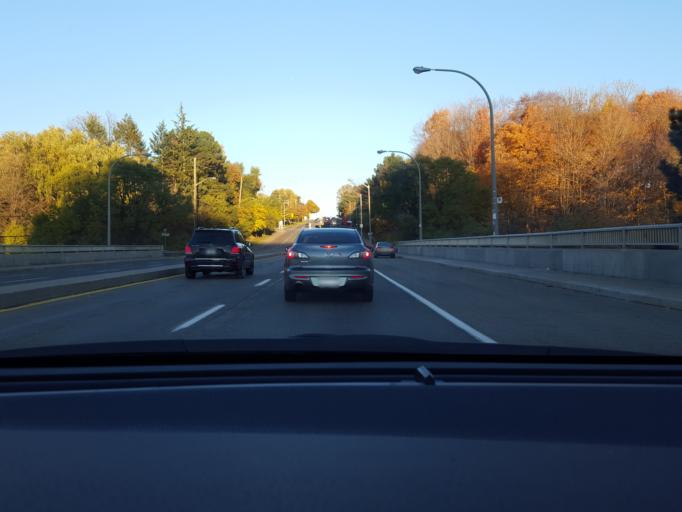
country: CA
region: Ontario
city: Willowdale
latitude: 43.7563
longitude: -79.3444
